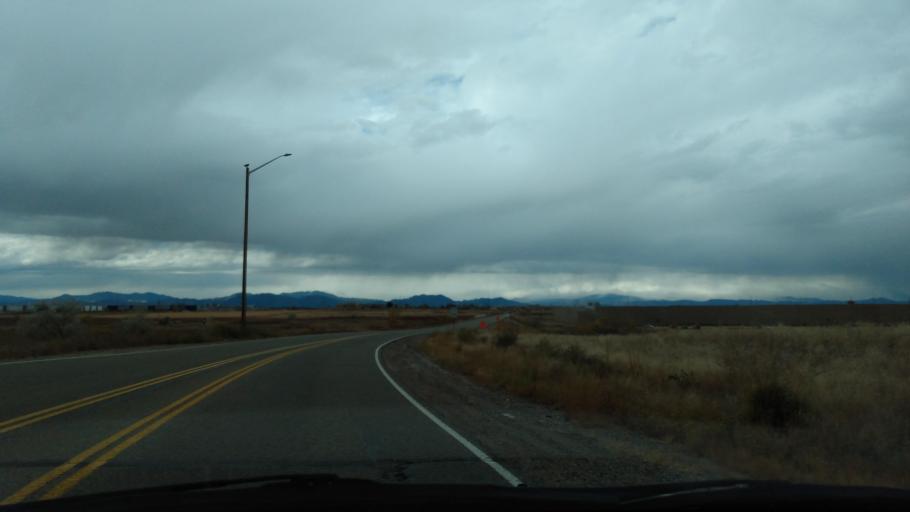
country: US
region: Colorado
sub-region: Adams County
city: Todd Creek
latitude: 39.9726
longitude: -104.9617
